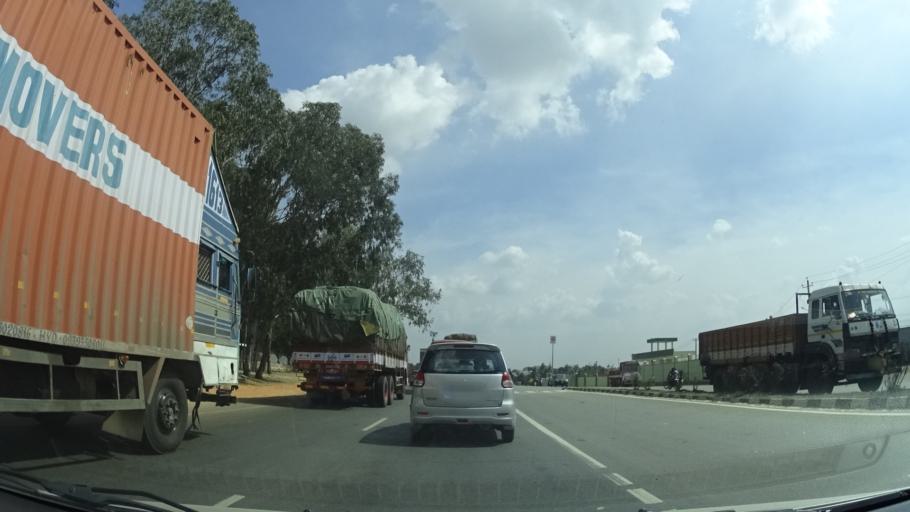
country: IN
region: Karnataka
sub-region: Bangalore Rural
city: Nelamangala
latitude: 13.1176
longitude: 77.3719
